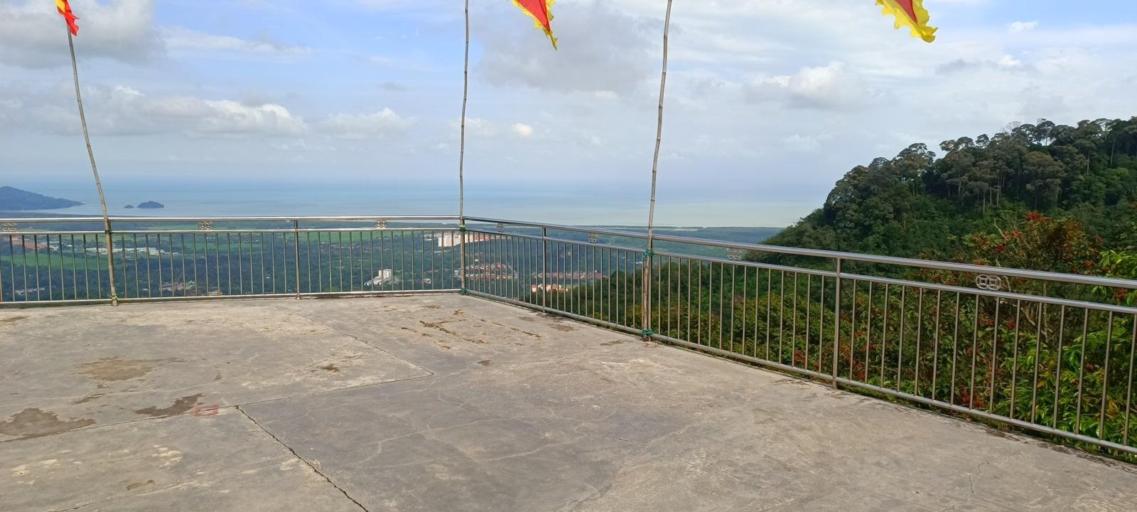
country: MY
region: Penang
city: Kampung Sungai Ara
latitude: 5.3767
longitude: 100.2438
